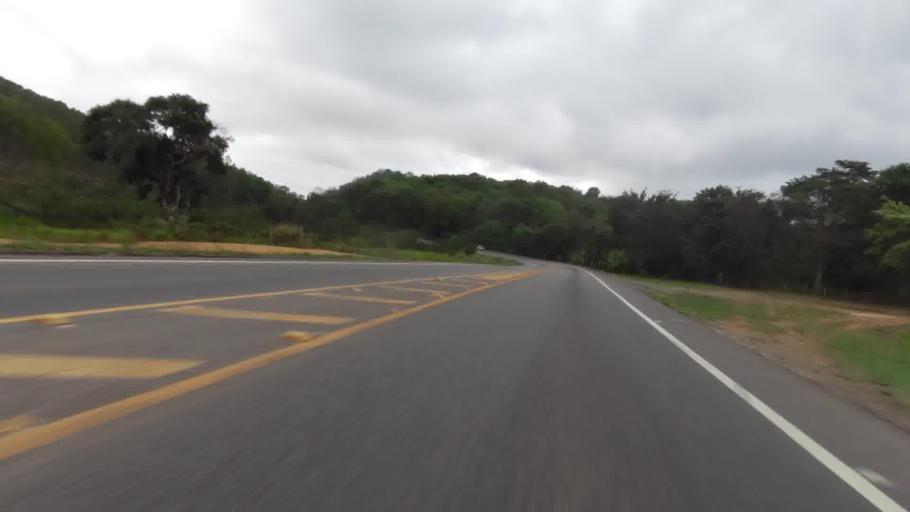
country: BR
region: Espirito Santo
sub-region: Alfredo Chaves
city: Alfredo Chaves
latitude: -20.7044
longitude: -40.7174
